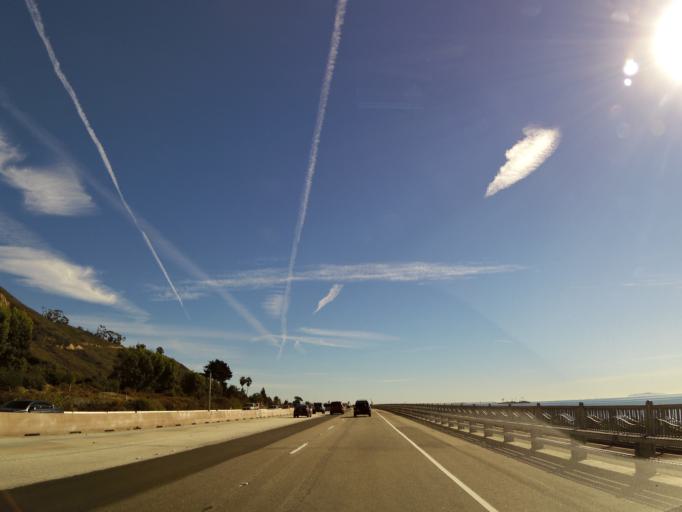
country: US
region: California
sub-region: Santa Barbara County
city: Carpinteria
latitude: 34.3672
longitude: -119.4525
